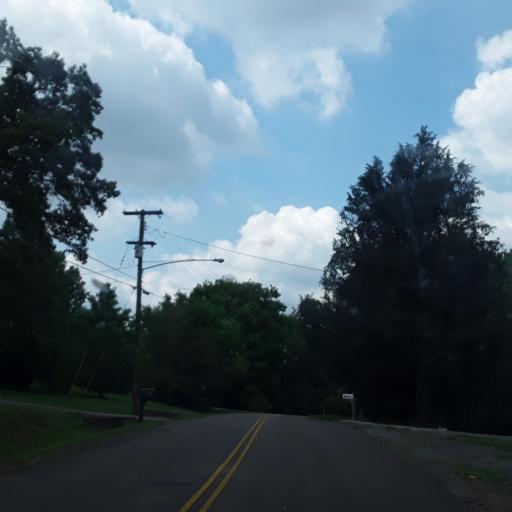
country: US
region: Tennessee
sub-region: Davidson County
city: Oak Hill
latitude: 36.1131
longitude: -86.7190
